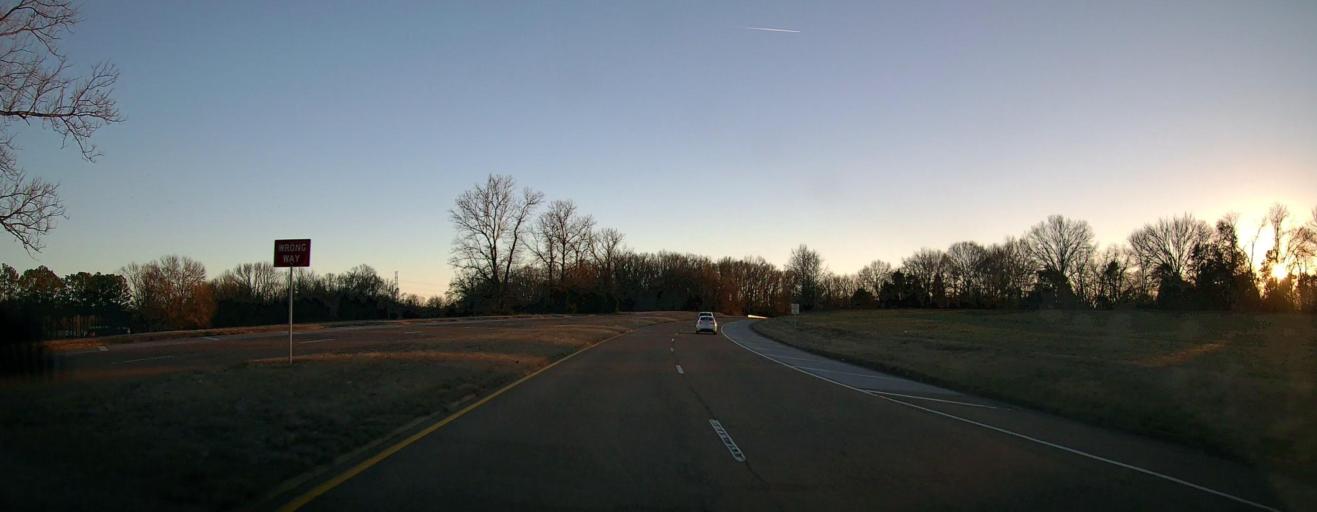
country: US
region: Tennessee
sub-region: Shelby County
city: Bartlett
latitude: 35.2607
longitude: -89.8895
